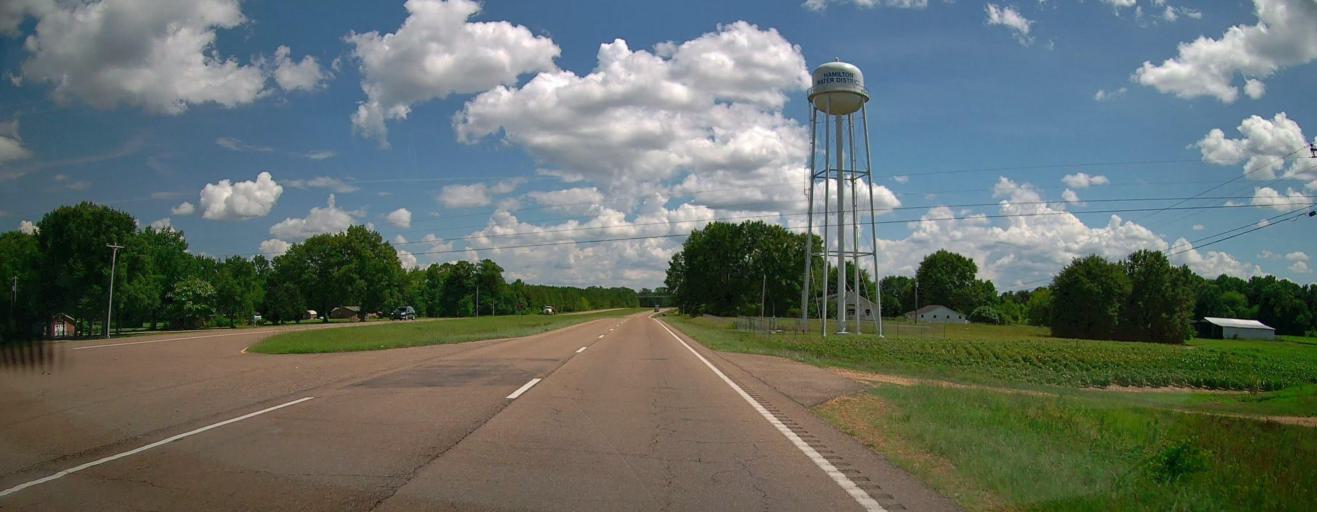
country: US
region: Mississippi
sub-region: Monroe County
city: Aberdeen
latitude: 33.7941
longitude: -88.4617
